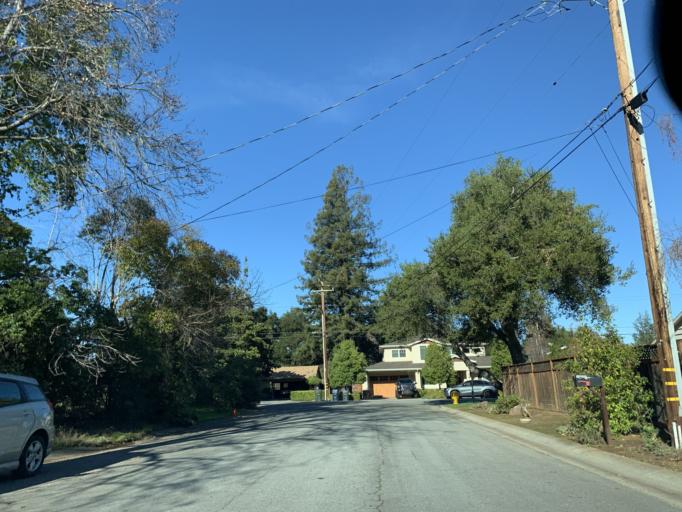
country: US
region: California
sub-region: Santa Clara County
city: Mountain View
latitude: 37.3821
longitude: -122.0984
